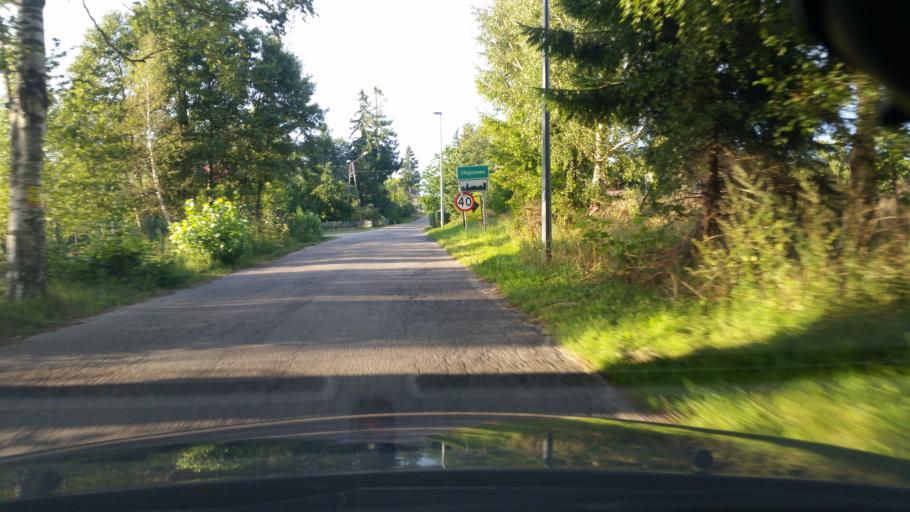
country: PL
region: Pomeranian Voivodeship
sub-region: Powiat wejherowski
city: Choczewo
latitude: 54.7671
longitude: 17.7935
